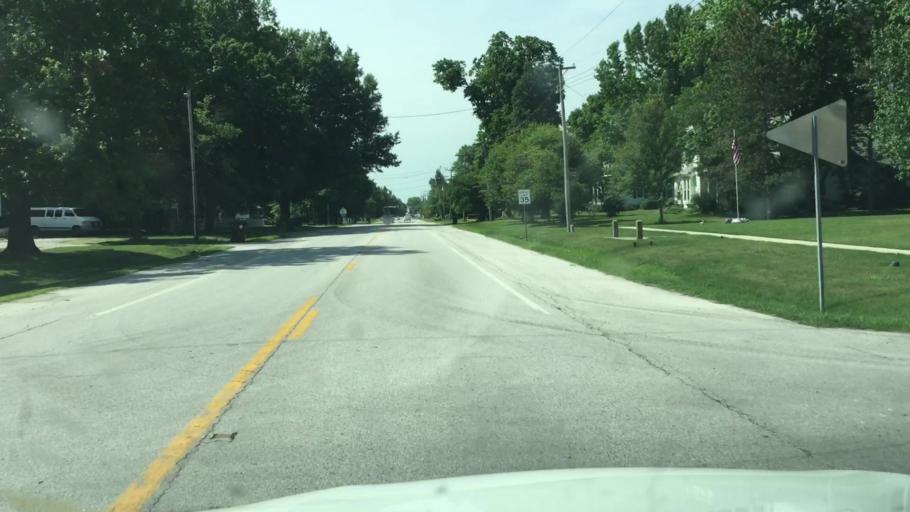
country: US
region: Illinois
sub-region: Hancock County
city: Carthage
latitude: 40.4206
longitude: -91.1362
